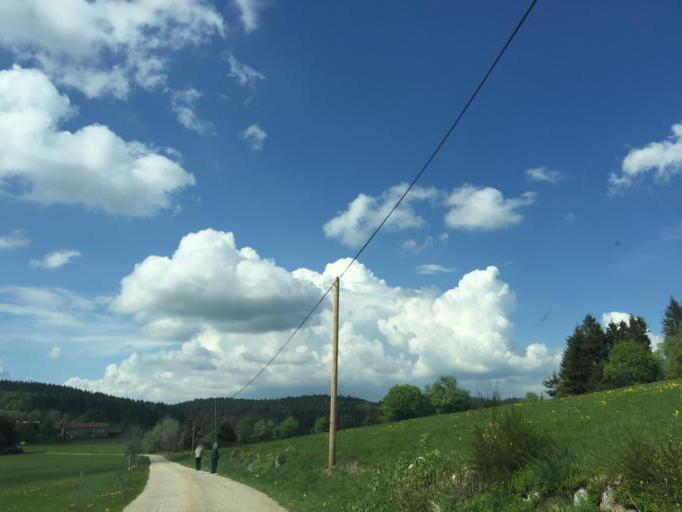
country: FR
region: Rhone-Alpes
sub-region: Departement de la Loire
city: Saint-Sauveur-en-Rue
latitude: 45.3026
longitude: 4.4787
